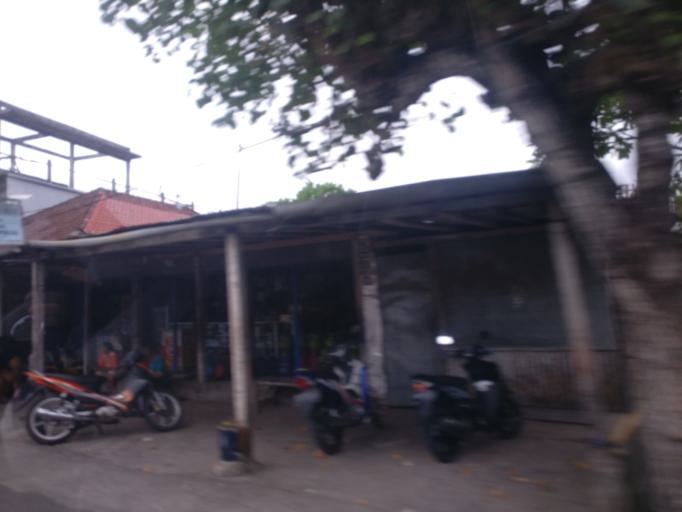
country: ID
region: Bali
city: Banjar Desa
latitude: -8.5743
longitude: 115.2965
